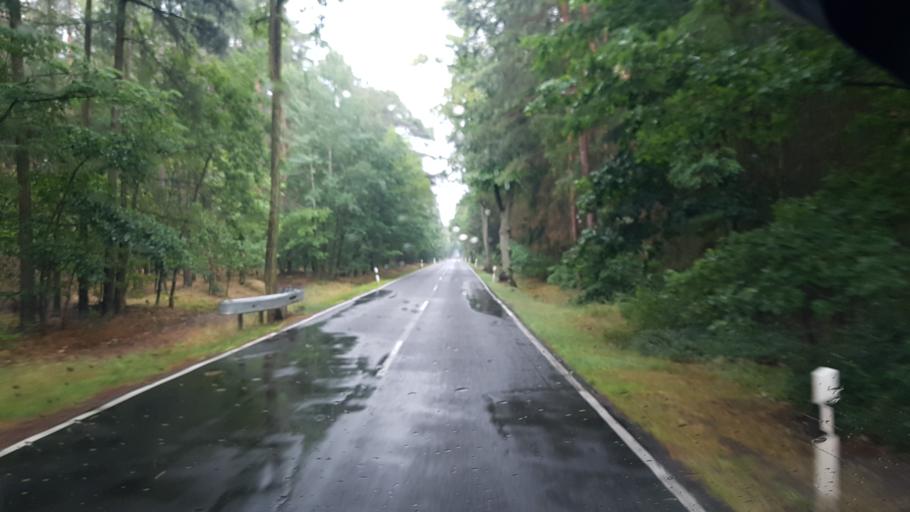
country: DE
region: Brandenburg
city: Dahme
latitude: 51.8423
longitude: 13.4127
